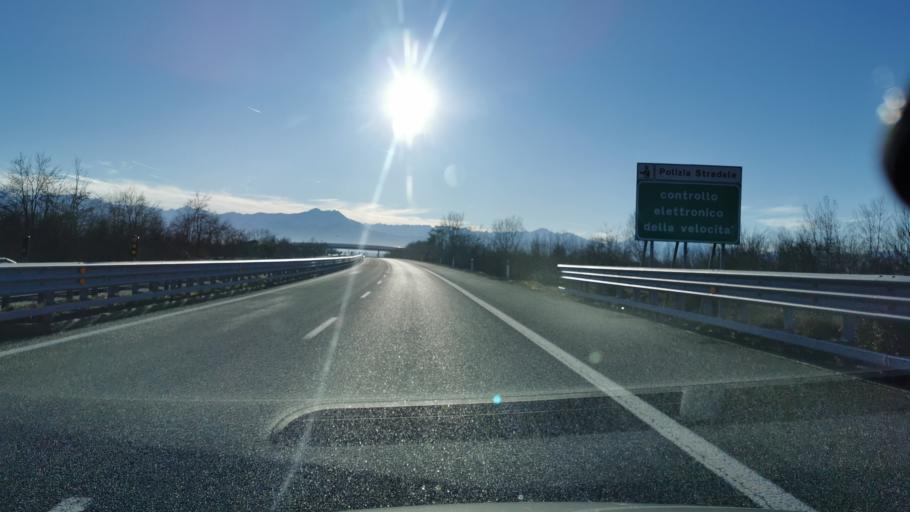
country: IT
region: Piedmont
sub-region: Provincia di Cuneo
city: Magliano Alpi
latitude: 44.4796
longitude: 7.7941
